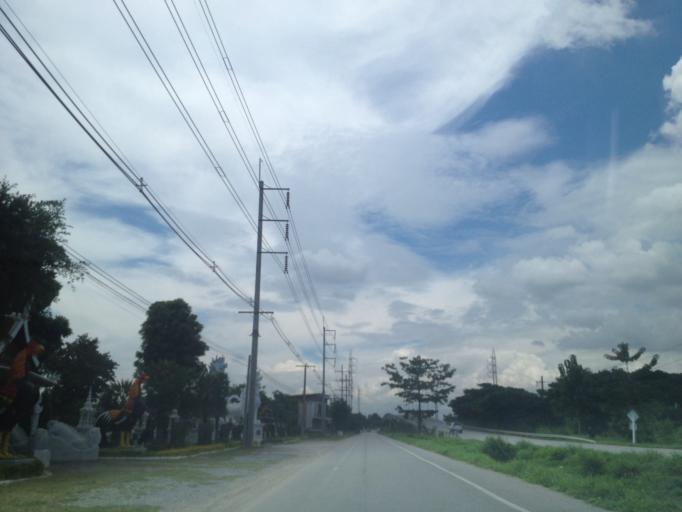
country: TH
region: Chiang Mai
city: Saraphi
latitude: 18.7200
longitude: 98.9828
